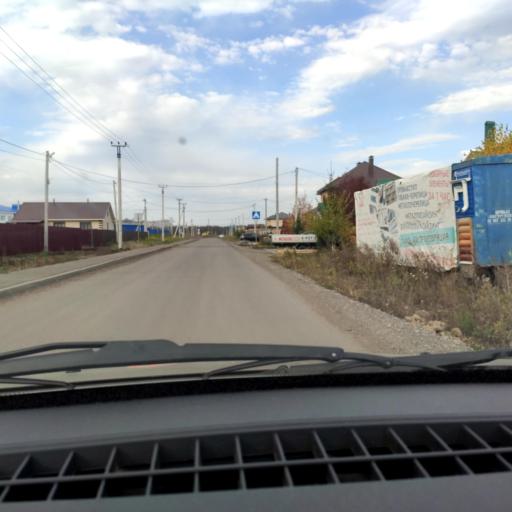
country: RU
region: Bashkortostan
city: Ufa
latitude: 54.6273
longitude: 55.9070
